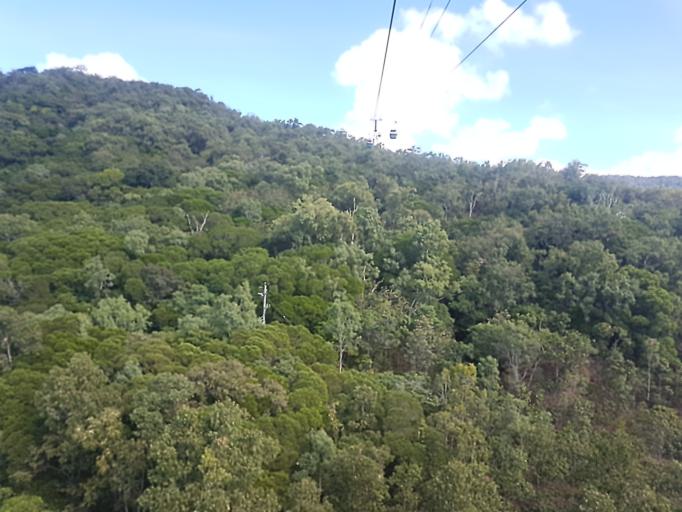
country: AU
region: Queensland
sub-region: Cairns
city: Redlynch
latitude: -16.8479
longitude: 145.6925
